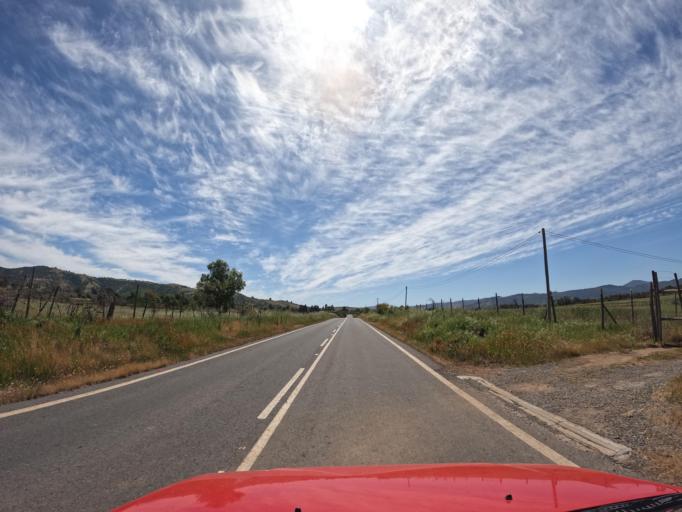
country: CL
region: Maule
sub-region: Provincia de Talca
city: Talca
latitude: -35.0340
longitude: -71.7598
